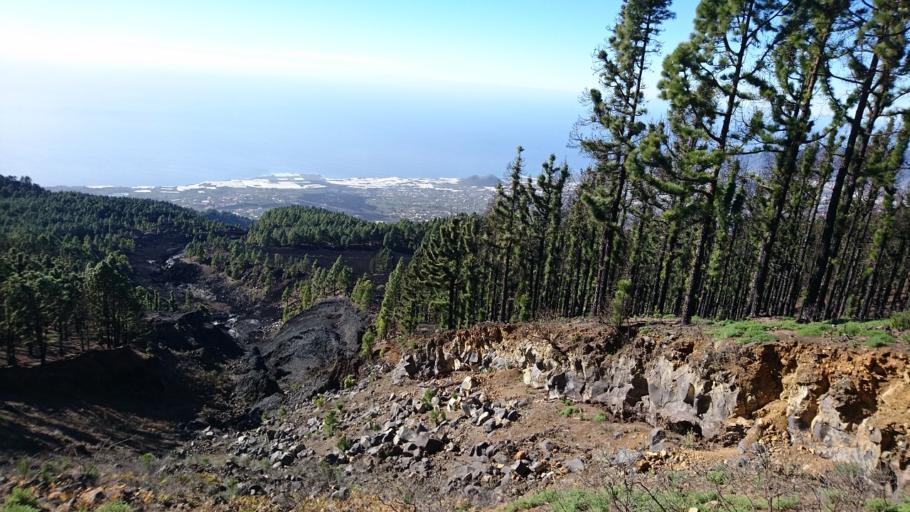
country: ES
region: Canary Islands
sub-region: Provincia de Santa Cruz de Tenerife
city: El Paso
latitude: 28.6024
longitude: -17.8533
